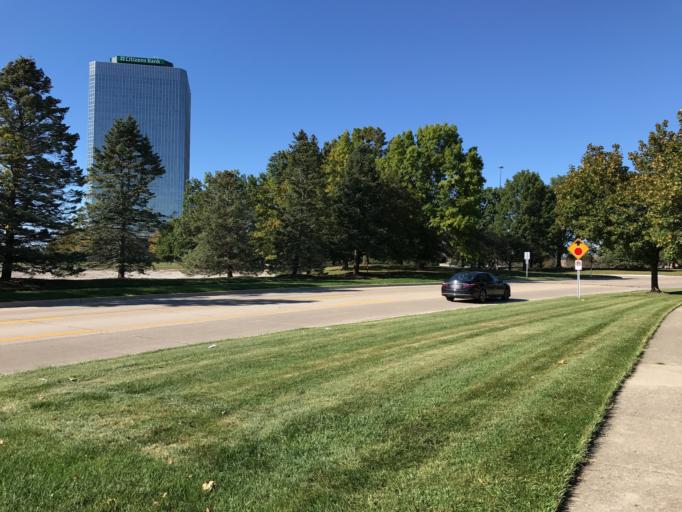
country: US
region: Michigan
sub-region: Oakland County
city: Franklin
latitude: 42.4883
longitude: -83.2964
